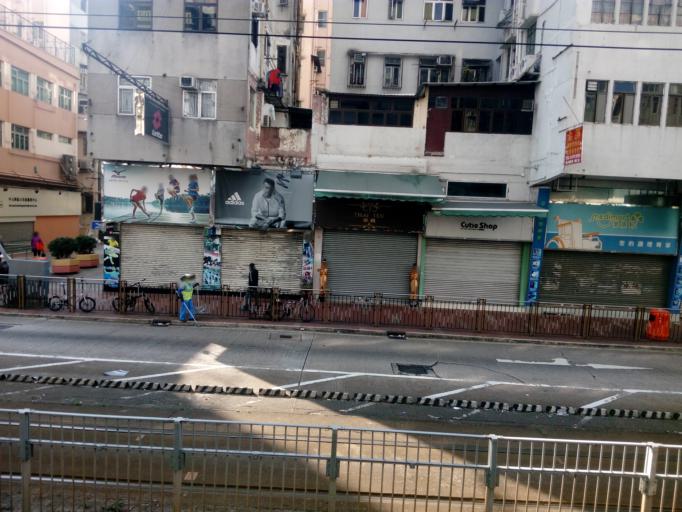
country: HK
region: Yuen Long
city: Yuen Long Kau Hui
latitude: 22.4444
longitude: 114.0248
